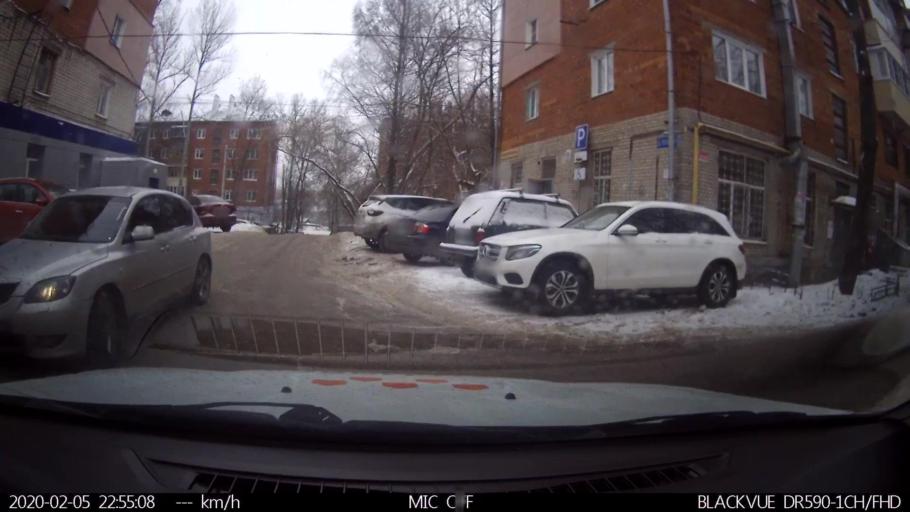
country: RU
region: Penza
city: Bogoslovka
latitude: 53.3364
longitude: 44.8134
